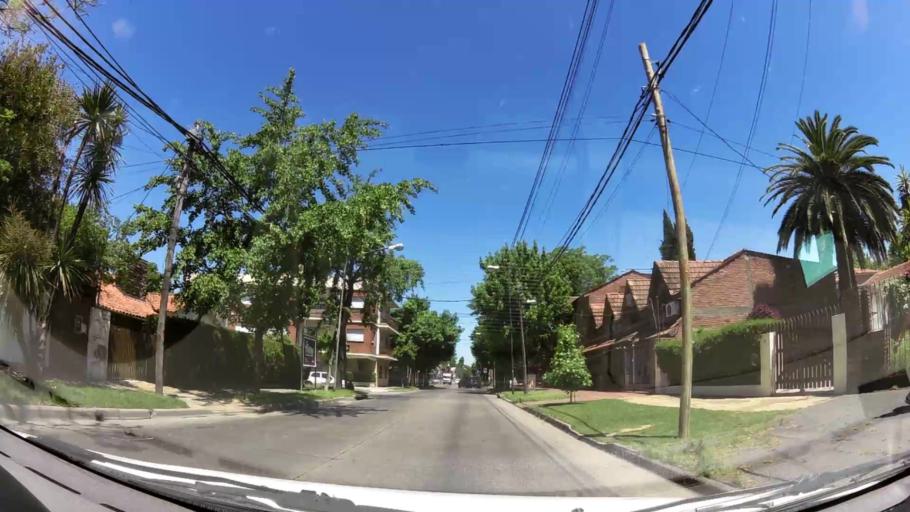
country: AR
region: Buenos Aires
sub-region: Partido de Vicente Lopez
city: Olivos
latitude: -34.5053
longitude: -58.5142
